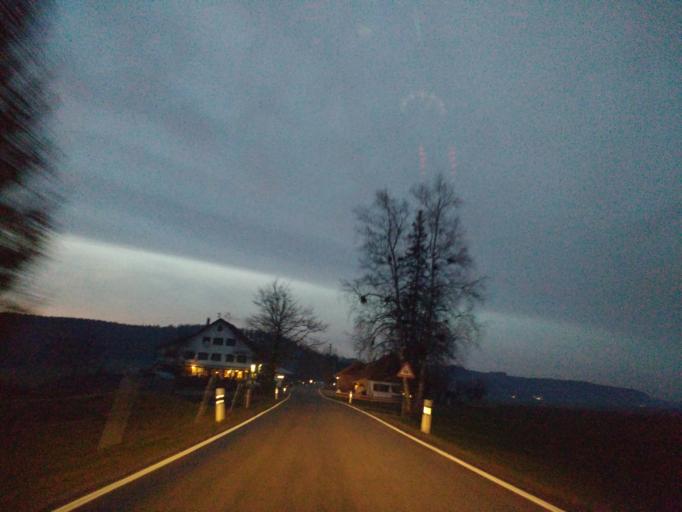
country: DE
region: Bavaria
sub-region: Swabia
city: Stottwang
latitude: 47.8623
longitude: 10.6947
